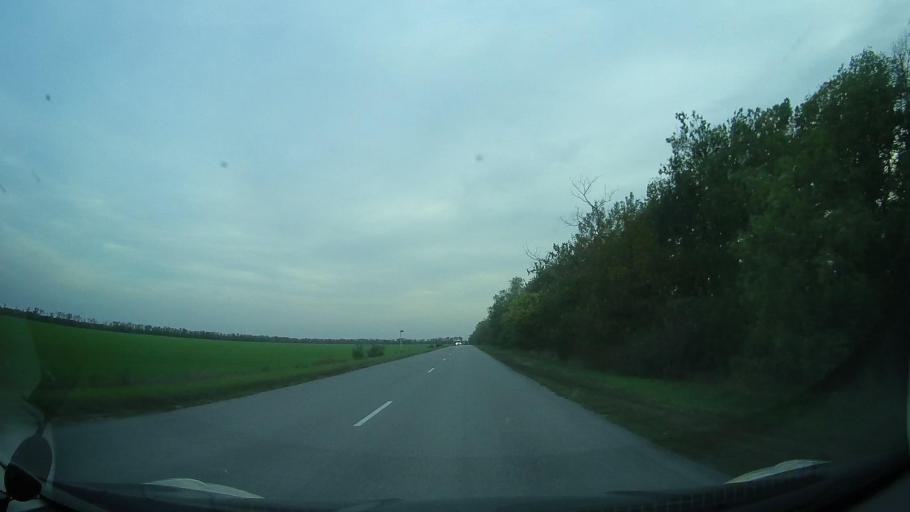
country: RU
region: Rostov
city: Kirovskaya
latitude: 47.0115
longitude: 39.9788
